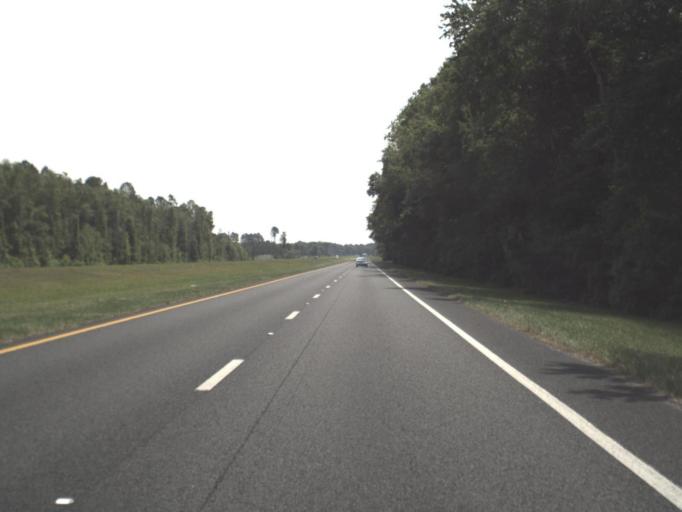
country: US
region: Florida
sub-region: Nassau County
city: Callahan
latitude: 30.6115
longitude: -81.7331
